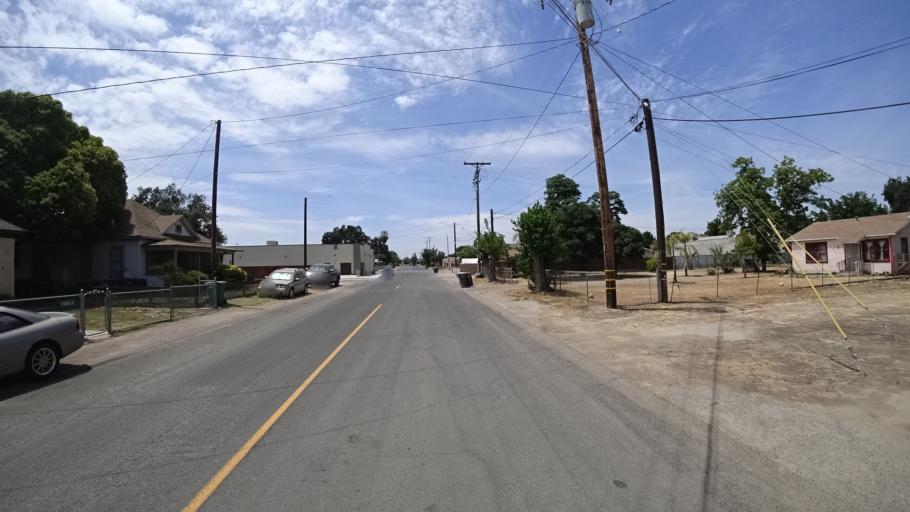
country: US
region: California
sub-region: Kings County
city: Armona
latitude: 36.3169
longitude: -119.7078
